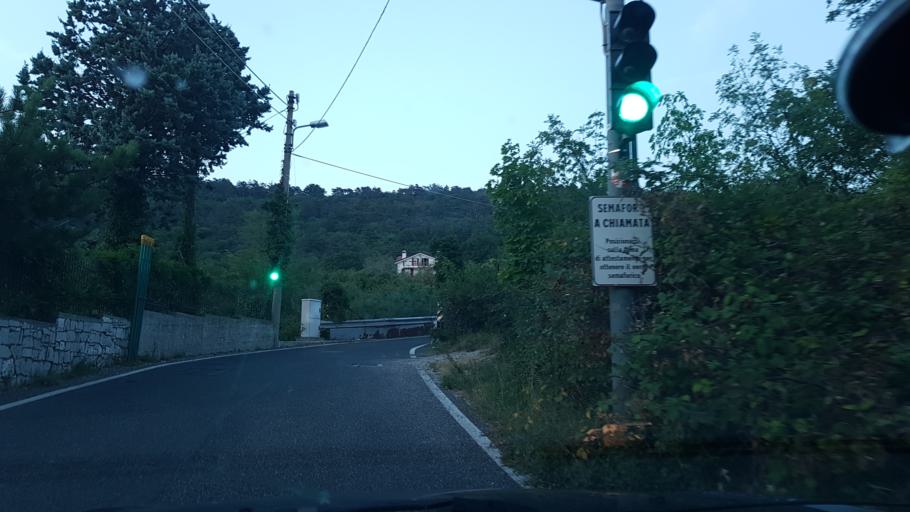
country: IT
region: Friuli Venezia Giulia
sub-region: Provincia di Trieste
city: Villa Opicina
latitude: 45.6791
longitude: 13.7713
